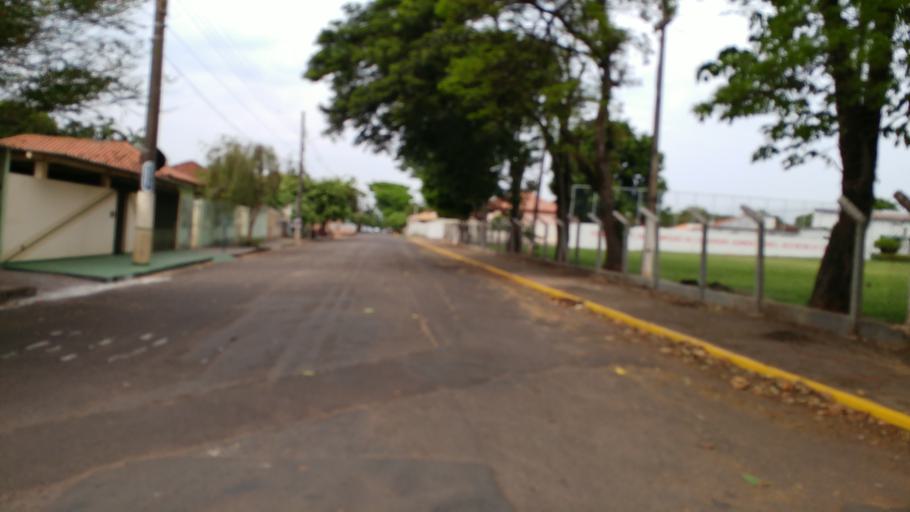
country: BR
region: Sao Paulo
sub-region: Paraguacu Paulista
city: Paraguacu Paulista
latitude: -22.4111
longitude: -50.5810
